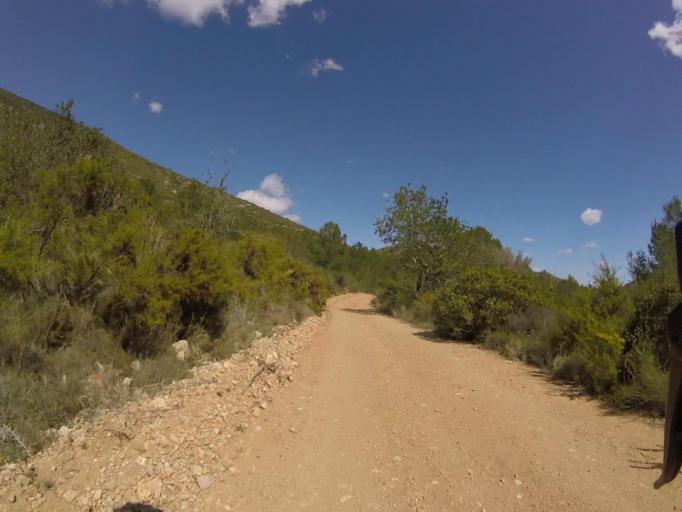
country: ES
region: Valencia
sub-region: Provincia de Castello
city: Cabanes
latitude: 40.1631
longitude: 0.1138
